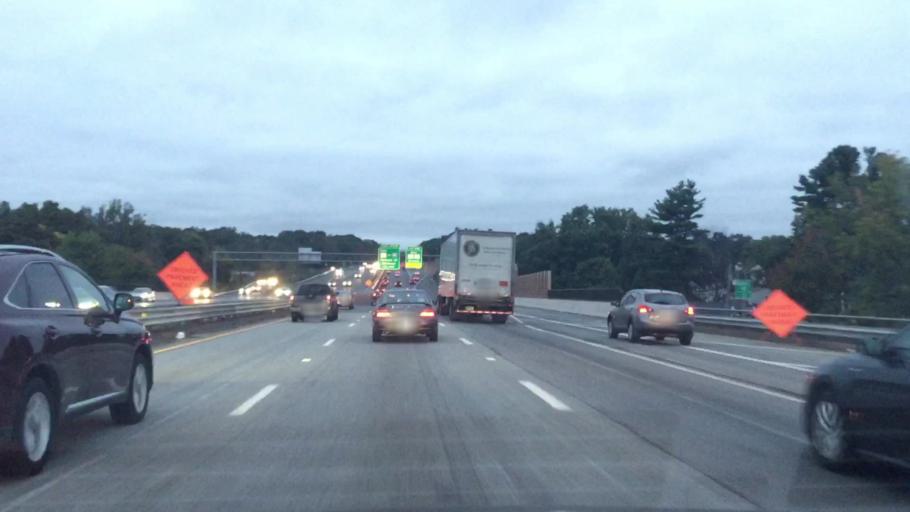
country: US
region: Massachusetts
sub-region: Essex County
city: Methuen
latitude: 42.7011
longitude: -71.2098
